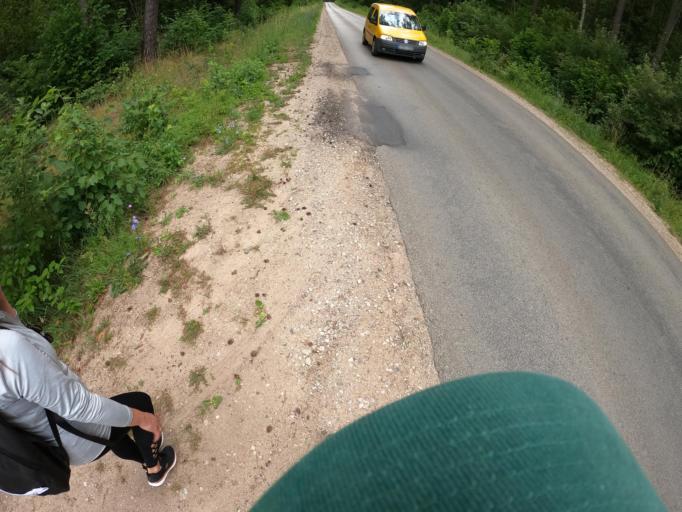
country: LT
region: Alytaus apskritis
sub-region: Alytus
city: Alytus
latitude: 54.4235
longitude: 24.0770
